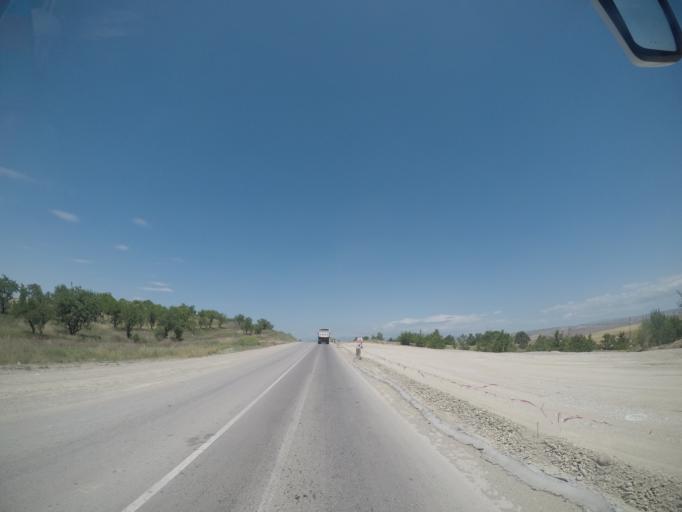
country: AZ
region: Qobustan
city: Qobustan
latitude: 40.5319
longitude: 48.7835
